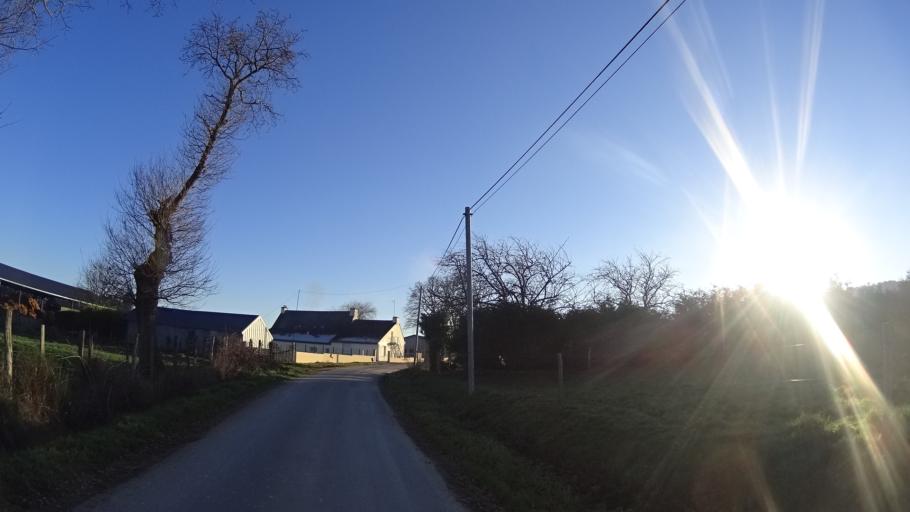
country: FR
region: Brittany
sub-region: Departement du Morbihan
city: Saint-Perreux
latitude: 47.6663
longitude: -2.1417
